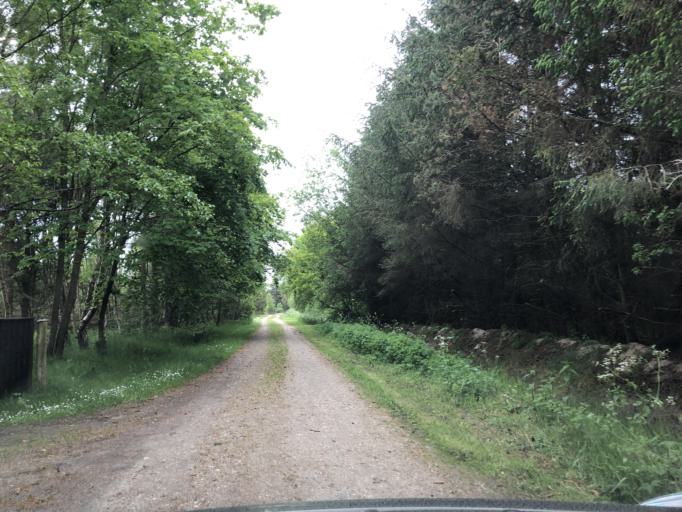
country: DK
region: Central Jutland
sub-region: Holstebro Kommune
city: Ulfborg
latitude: 56.2742
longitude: 8.1647
